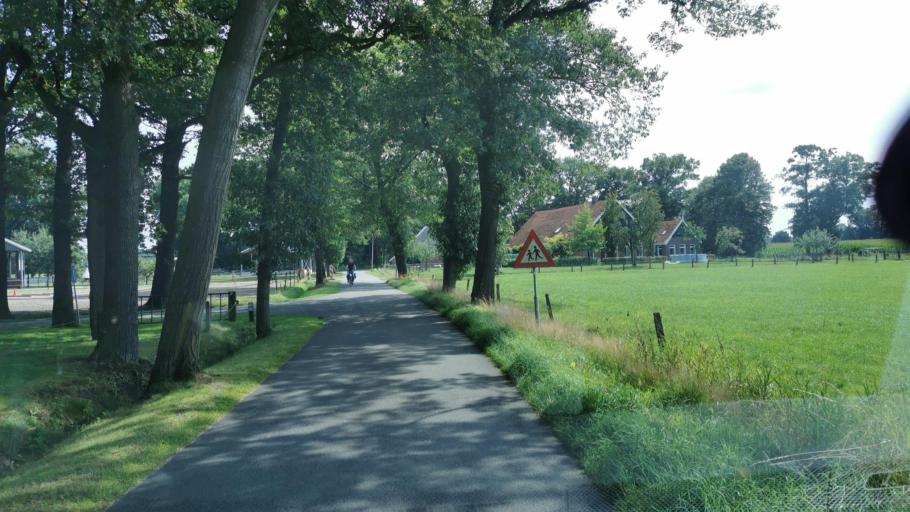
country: NL
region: Overijssel
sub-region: Gemeente Enschede
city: Enschede
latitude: 52.1736
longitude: 6.8957
